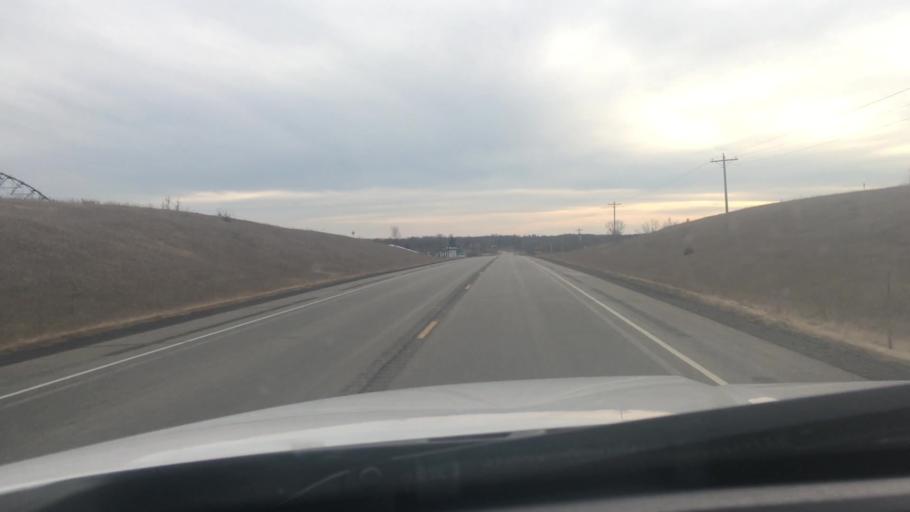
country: US
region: Minnesota
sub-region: Otter Tail County
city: Perham
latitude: 46.3063
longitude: -95.7183
